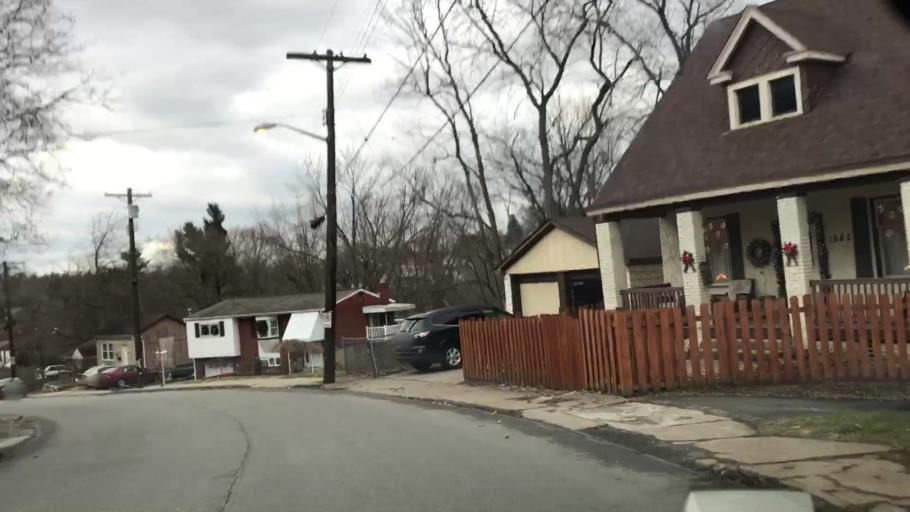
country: US
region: Pennsylvania
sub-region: Allegheny County
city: Ingram
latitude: 40.4425
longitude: -80.0527
